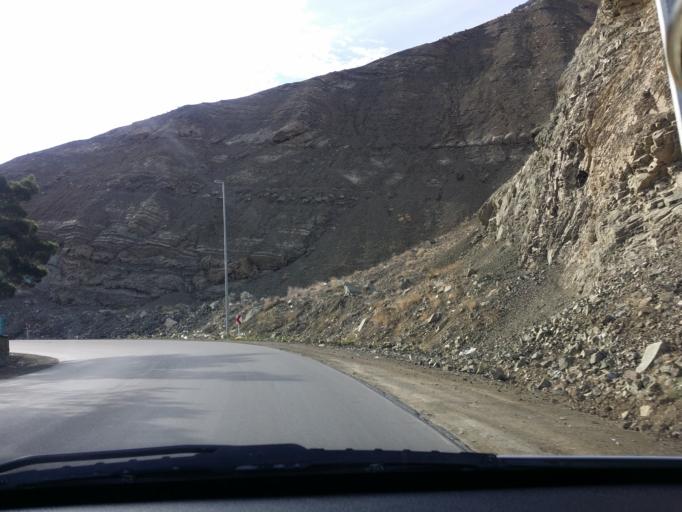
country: IR
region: Alborz
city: Karaj
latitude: 35.9695
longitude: 51.0935
